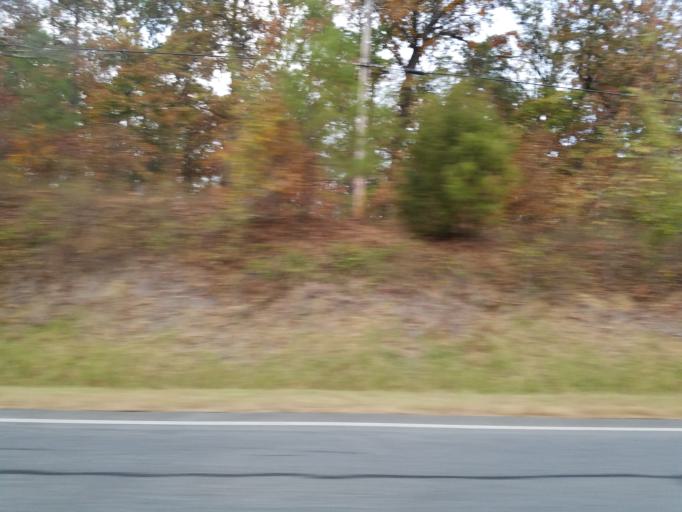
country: US
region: Georgia
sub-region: Murray County
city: Chatsworth
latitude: 34.6038
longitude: -84.7977
